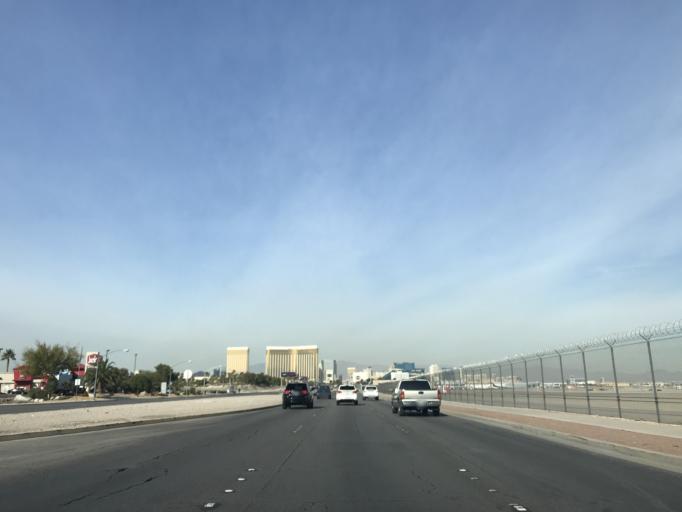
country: US
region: Nevada
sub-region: Clark County
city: Paradise
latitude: 36.0730
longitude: -115.1724
